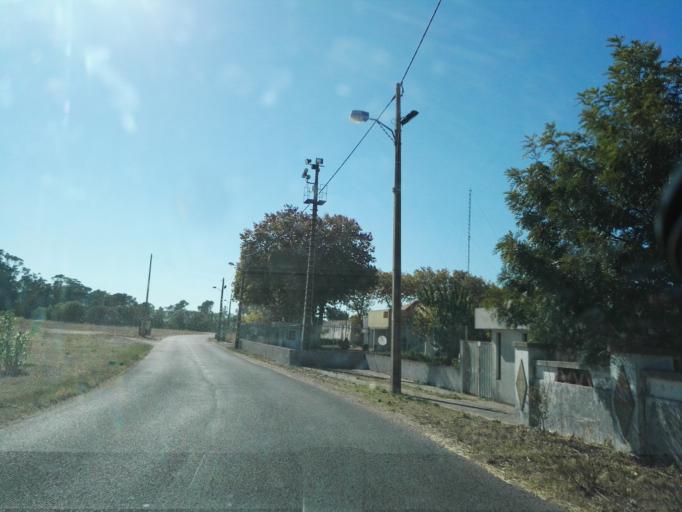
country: PT
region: Lisbon
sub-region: Odivelas
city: Pontinha
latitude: 38.7334
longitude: -9.1912
